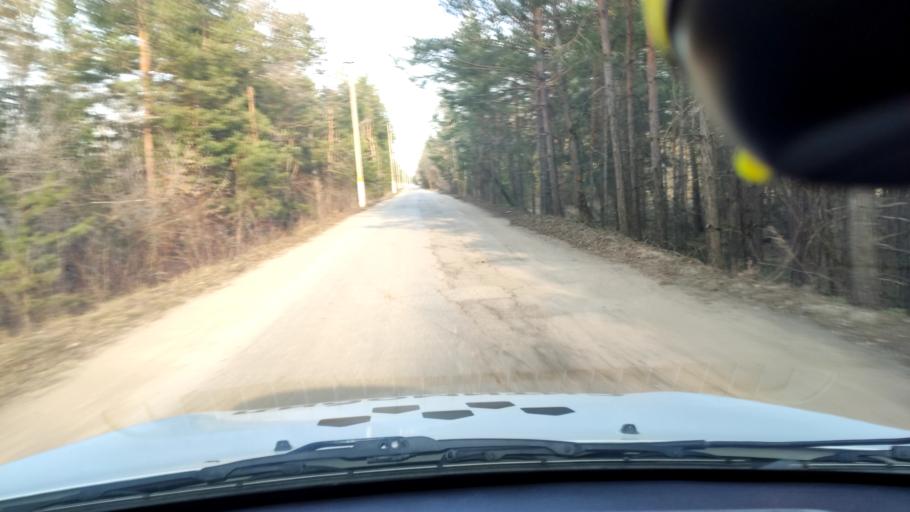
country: RU
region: Samara
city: Zhigulevsk
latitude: 53.4584
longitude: 49.6110
